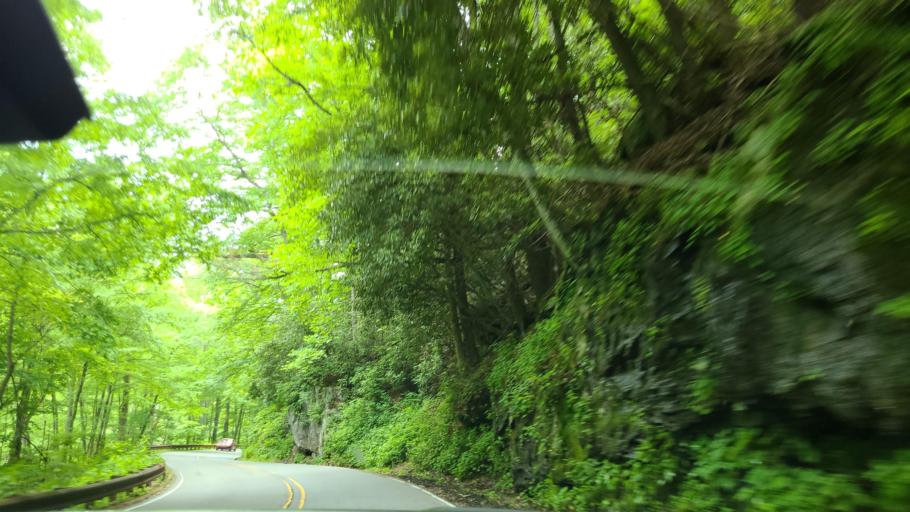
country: US
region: North Carolina
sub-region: Macon County
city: Franklin
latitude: 35.0826
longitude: -83.2638
